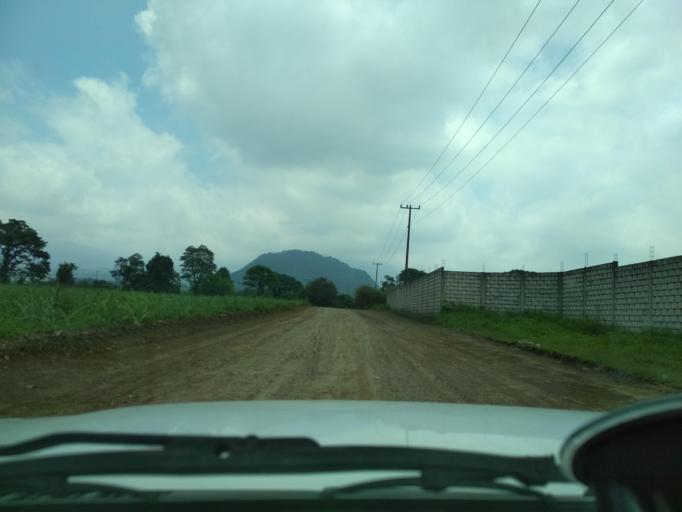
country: MX
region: Veracruz
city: Atzacan
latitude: 18.8805
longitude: -97.0792
